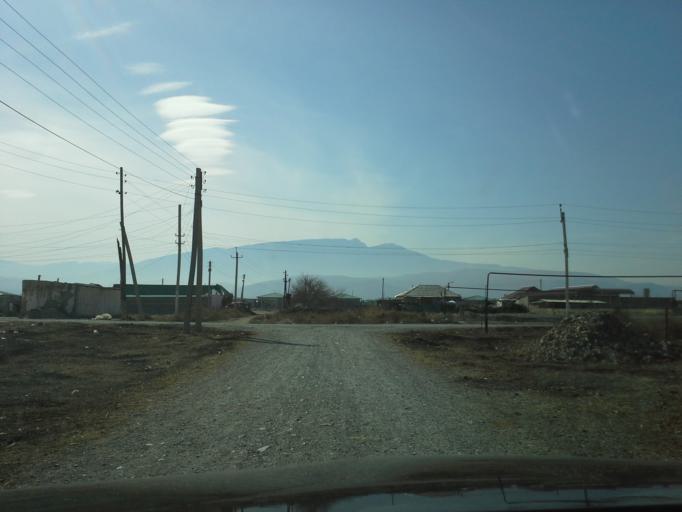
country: TM
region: Ahal
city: Abadan
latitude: 38.1050
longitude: 58.0315
